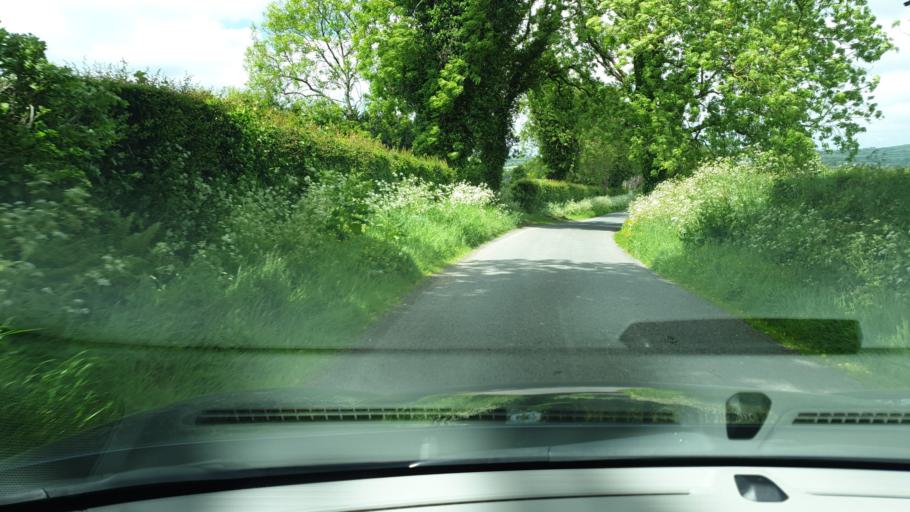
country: IE
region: Leinster
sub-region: An Mhi
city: Slane
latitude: 53.7388
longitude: -6.5629
